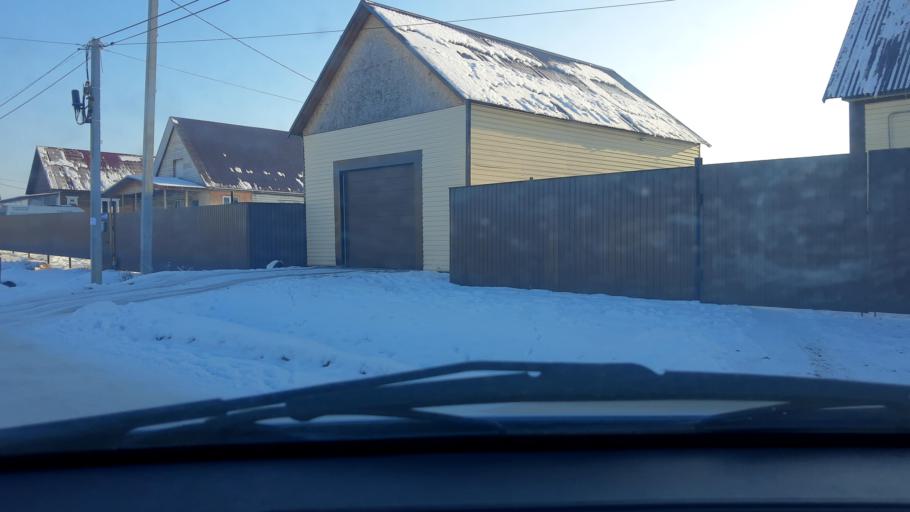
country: RU
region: Bashkortostan
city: Iglino
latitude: 54.8021
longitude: 56.3893
